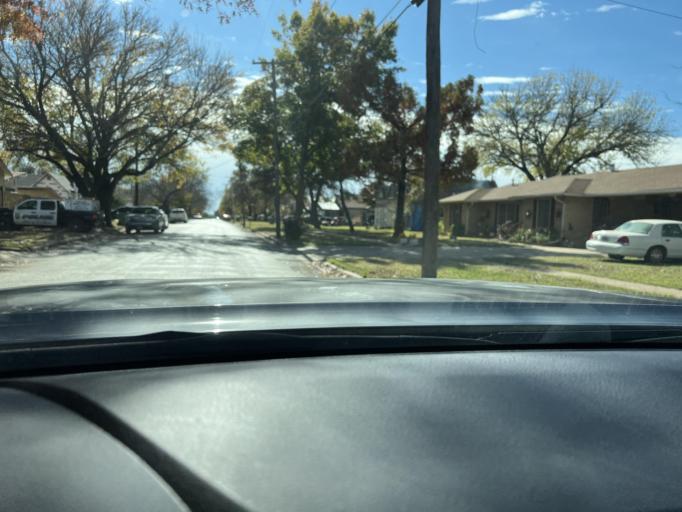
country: US
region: Texas
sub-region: Eastland County
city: Eastland
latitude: 32.3980
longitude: -98.8216
